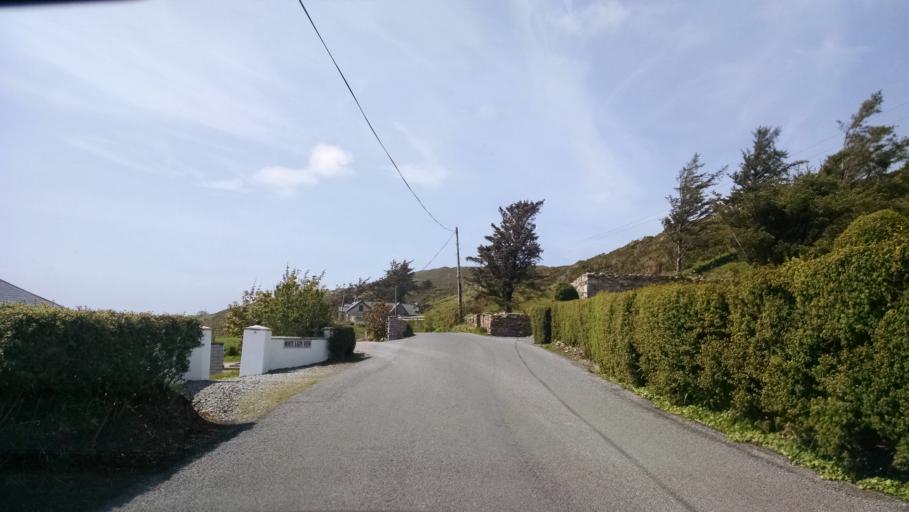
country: IE
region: Connaught
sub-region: County Galway
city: Clifden
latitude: 53.4934
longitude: -10.0521
